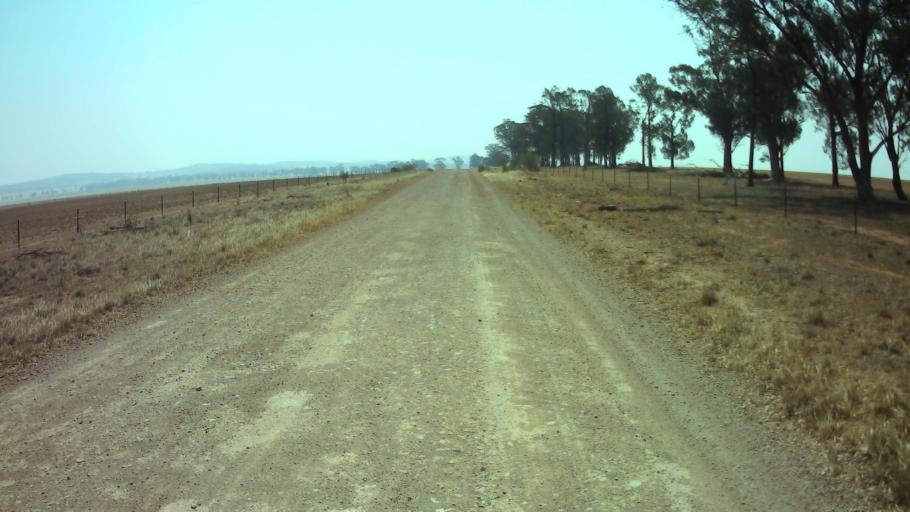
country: AU
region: New South Wales
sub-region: Weddin
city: Grenfell
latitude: -33.6372
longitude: 148.2266
